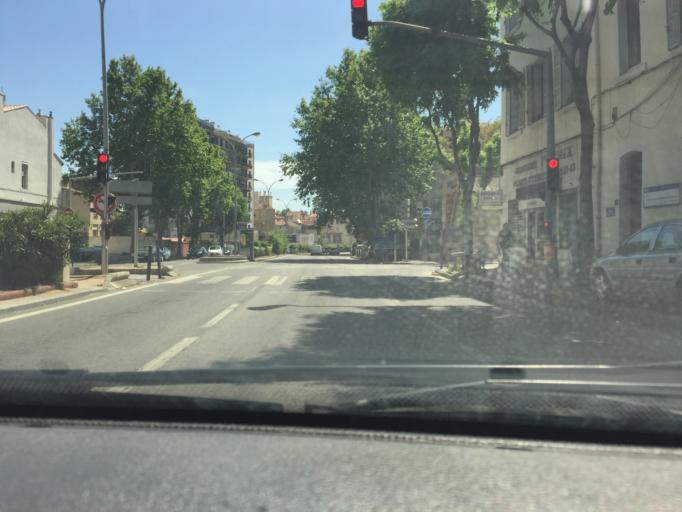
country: FR
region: Provence-Alpes-Cote d'Azur
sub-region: Departement des Bouches-du-Rhone
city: Marseille 04
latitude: 43.3098
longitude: 5.4030
